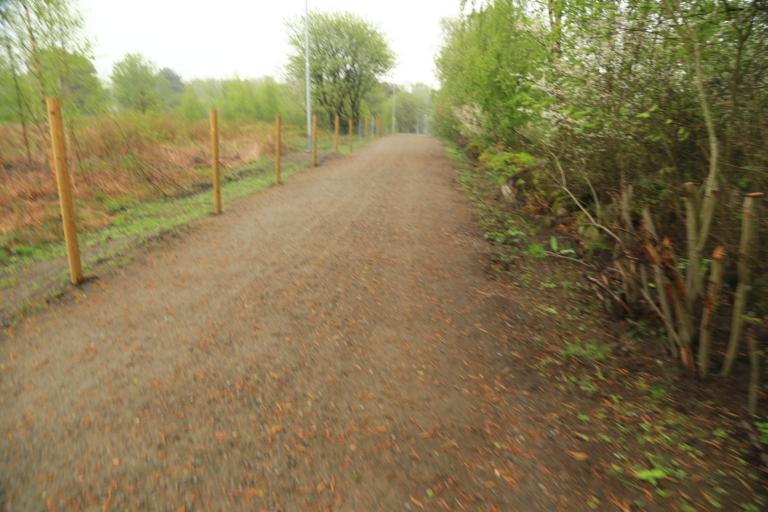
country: SE
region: Halland
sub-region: Varbergs Kommun
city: Varberg
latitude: 57.0911
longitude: 12.2724
